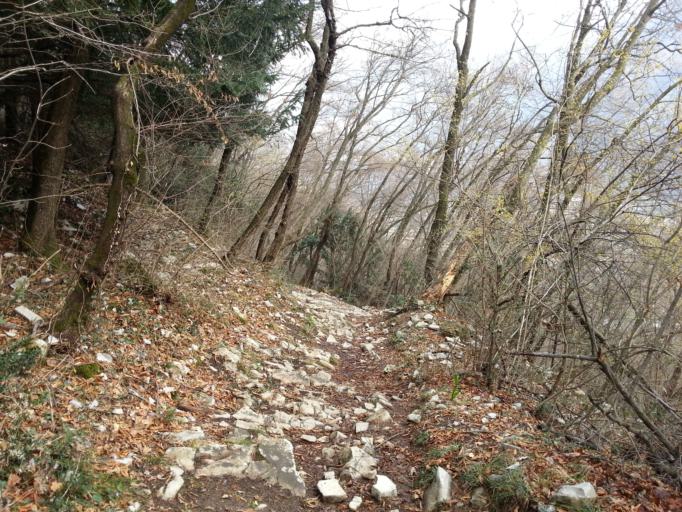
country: CH
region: Ticino
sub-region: Mendrisio District
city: Riva San Vitale
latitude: 45.8930
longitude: 8.9619
